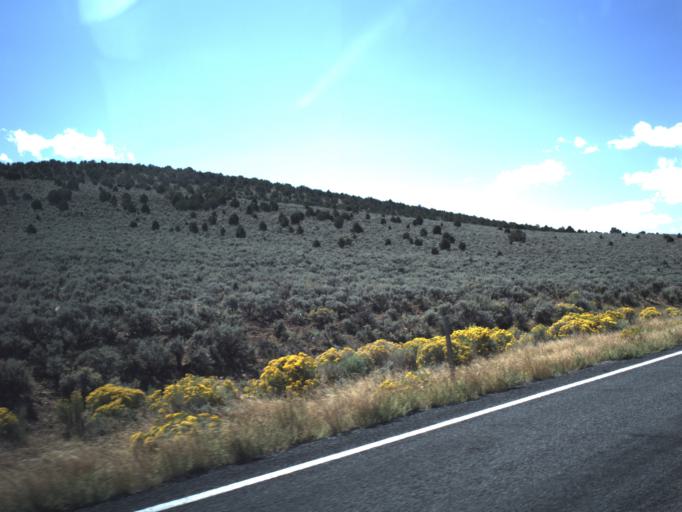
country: US
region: Utah
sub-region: Iron County
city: Parowan
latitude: 38.0522
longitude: -112.9771
